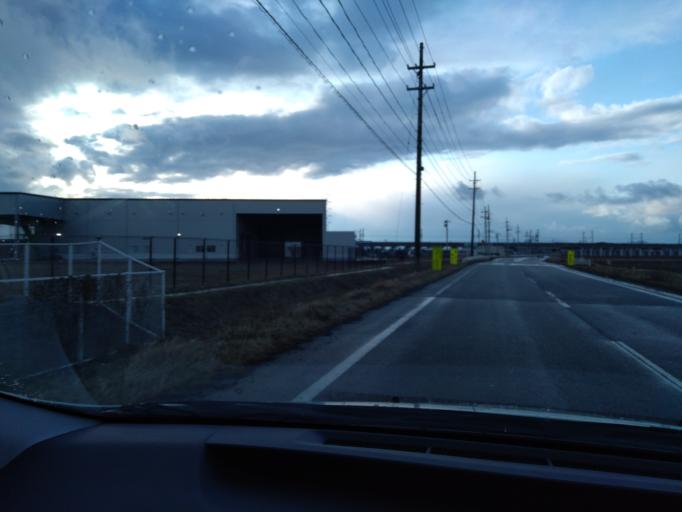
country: JP
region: Iwate
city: Ichinoseki
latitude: 38.7897
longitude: 141.0975
